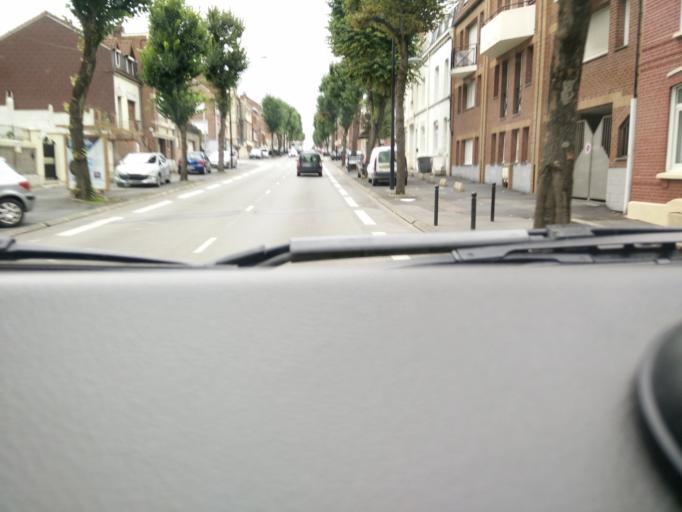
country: FR
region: Nord-Pas-de-Calais
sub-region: Departement du Nord
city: Anzin
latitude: 50.3541
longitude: 3.5092
